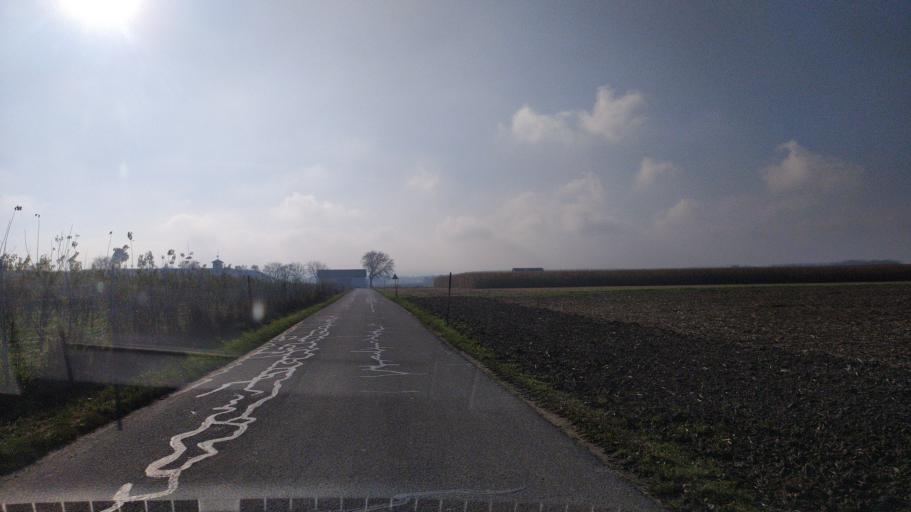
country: AT
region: Upper Austria
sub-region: Politischer Bezirk Perg
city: Perg
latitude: 48.1987
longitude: 14.6518
